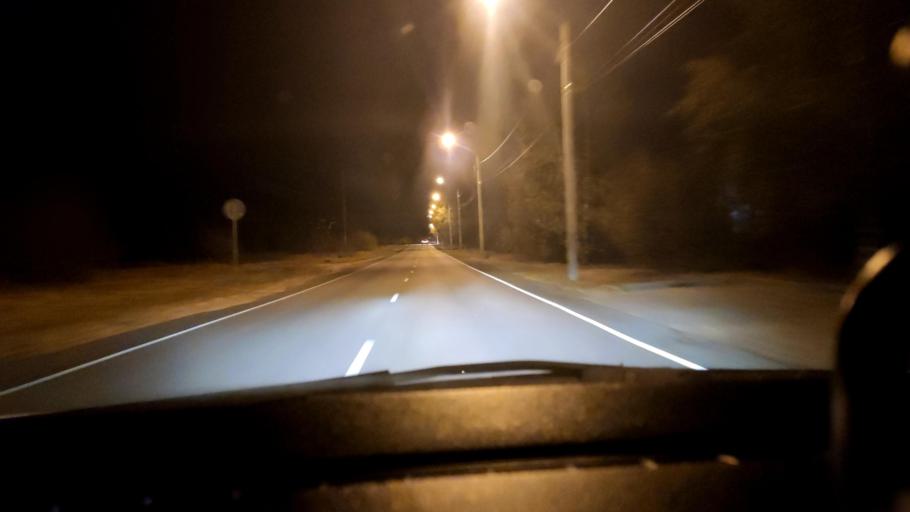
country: RU
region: Voronezj
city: Pridonskoy
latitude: 51.6138
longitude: 39.0536
